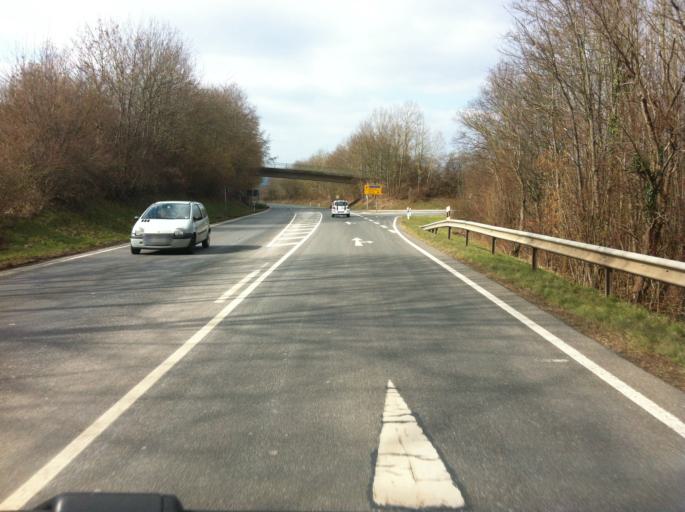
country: DE
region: North Rhine-Westphalia
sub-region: Regierungsbezirk Koln
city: Mechernich
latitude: 50.5704
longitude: 6.6971
